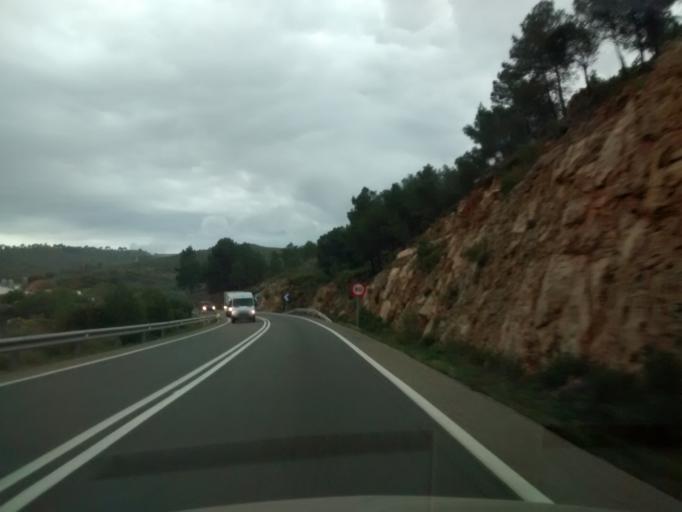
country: ES
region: Catalonia
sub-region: Provincia de Tarragona
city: Gandesa
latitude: 41.0401
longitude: 0.4697
